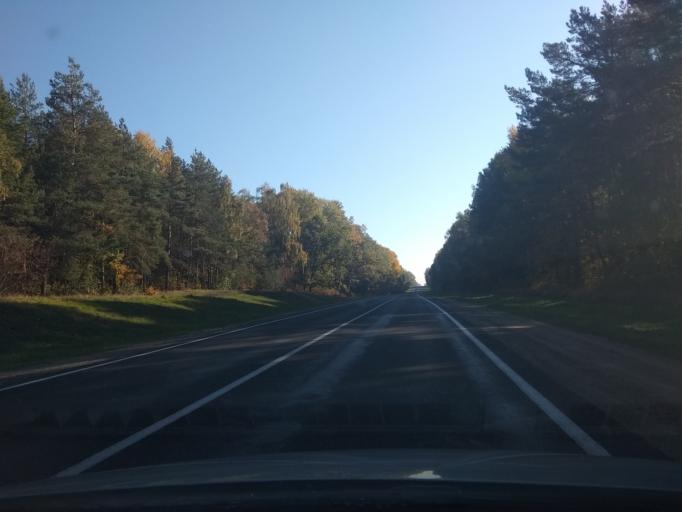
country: BY
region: Grodnenskaya
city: Zel'va
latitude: 53.1414
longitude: 24.8946
